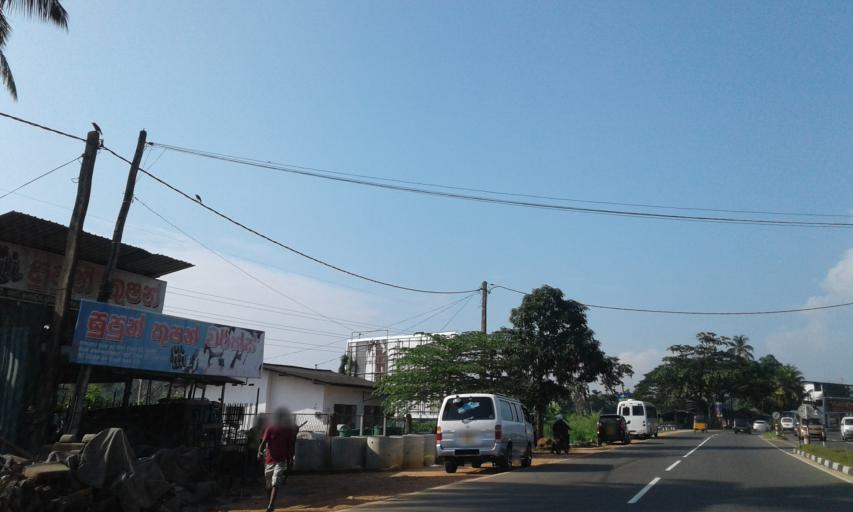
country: LK
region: Western
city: Gampaha
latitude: 7.0477
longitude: 80.0002
